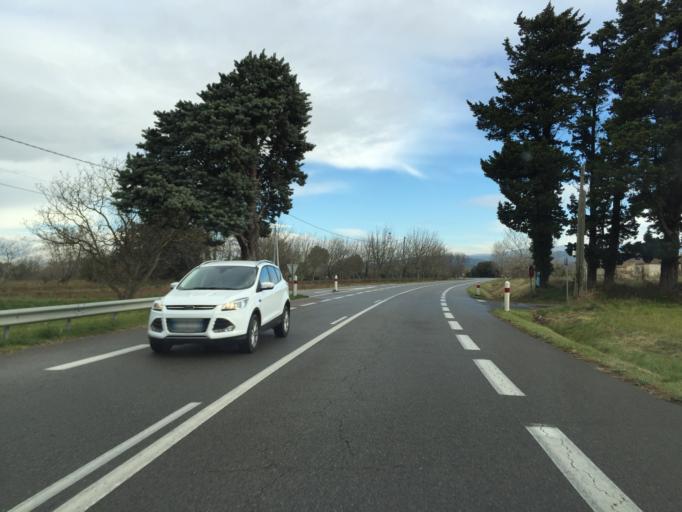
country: FR
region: Provence-Alpes-Cote d'Azur
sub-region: Departement du Vaucluse
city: Velleron
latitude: 43.9802
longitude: 5.0088
